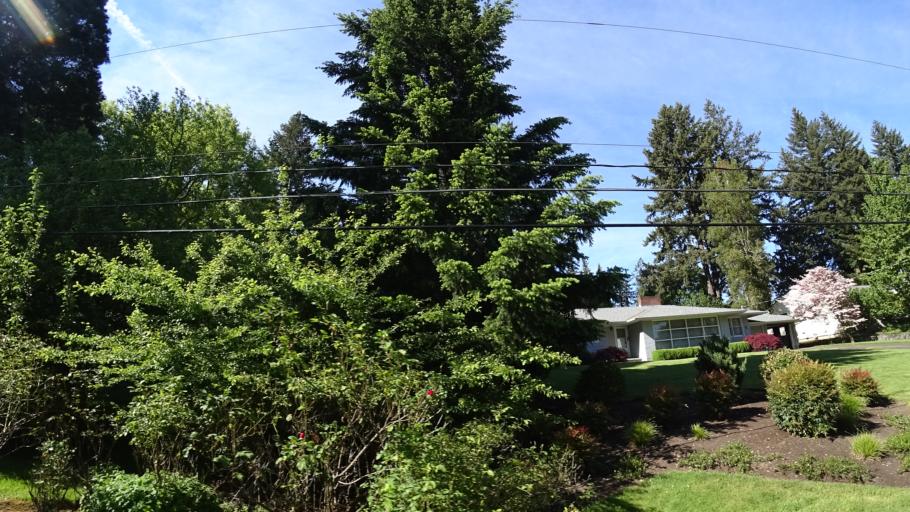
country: US
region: Oregon
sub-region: Washington County
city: West Slope
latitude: 45.4923
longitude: -122.7535
